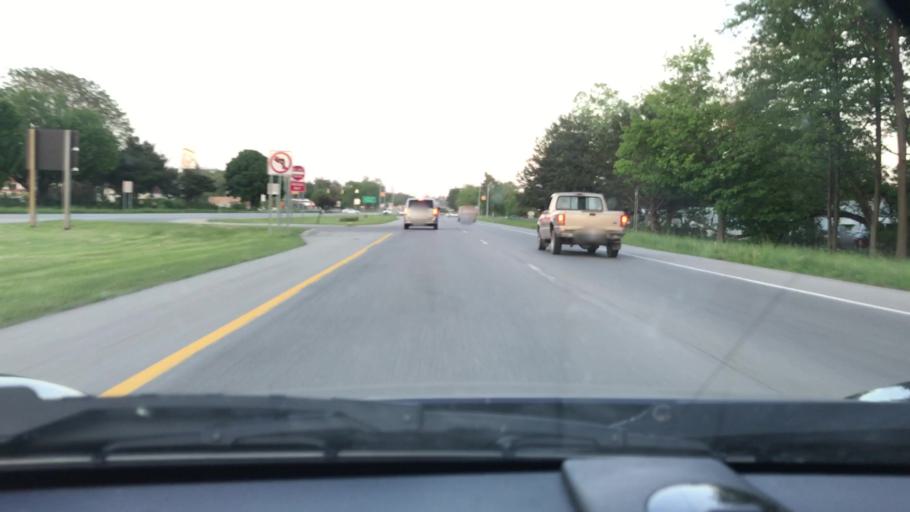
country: US
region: Michigan
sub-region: Muskegon County
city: Muskegon Heights
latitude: 43.1893
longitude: -86.2437
